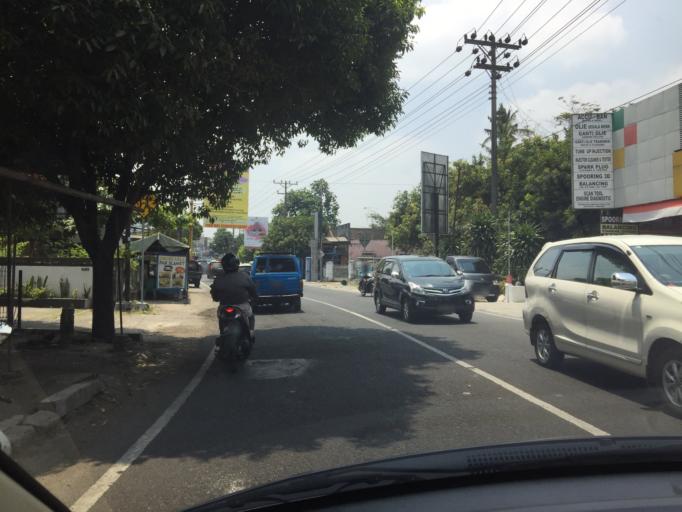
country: ID
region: Daerah Istimewa Yogyakarta
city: Melati
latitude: -7.7499
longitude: 110.3718
